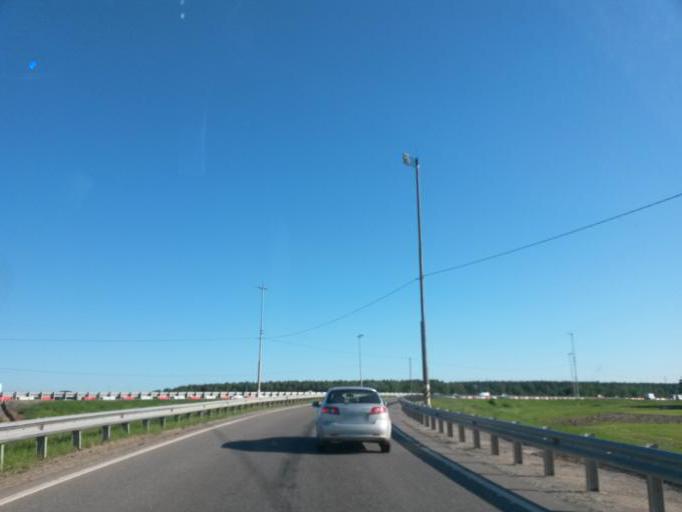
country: RU
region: Moskovskaya
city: L'vovskiy
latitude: 55.3331
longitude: 37.5708
